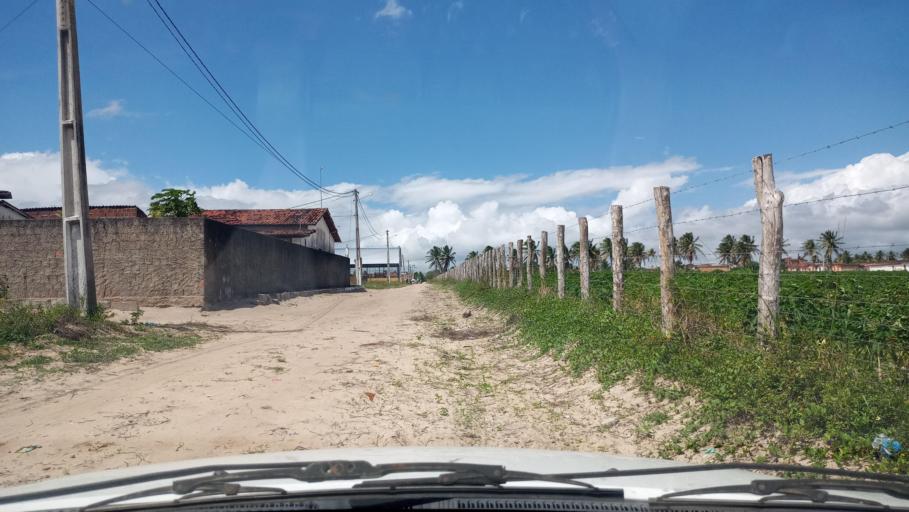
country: BR
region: Rio Grande do Norte
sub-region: Brejinho
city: Brejinho
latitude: -6.1921
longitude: -35.3669
